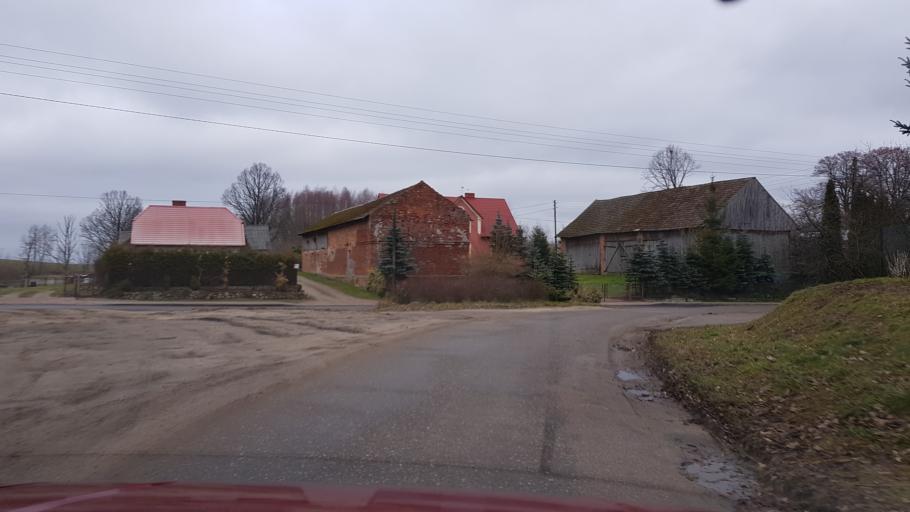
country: PL
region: Pomeranian Voivodeship
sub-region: Powiat bytowski
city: Borzytuchom
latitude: 54.1635
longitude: 17.3452
